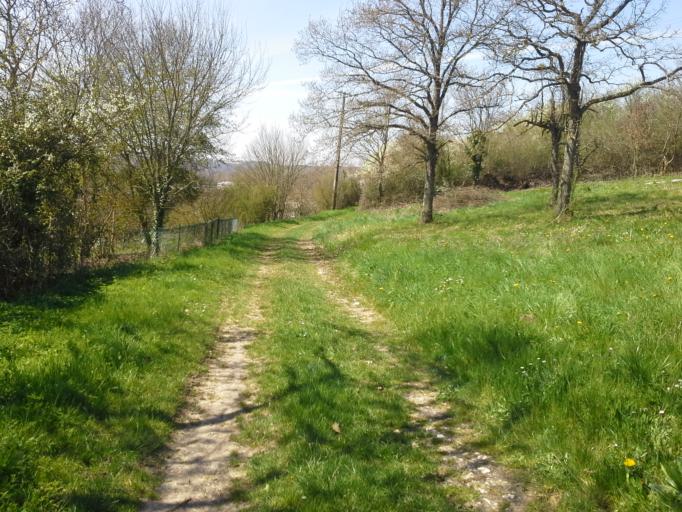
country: FR
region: Centre
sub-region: Departement du Loir-et-Cher
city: Villiers-sur-Loir
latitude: 47.8096
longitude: 0.9894
